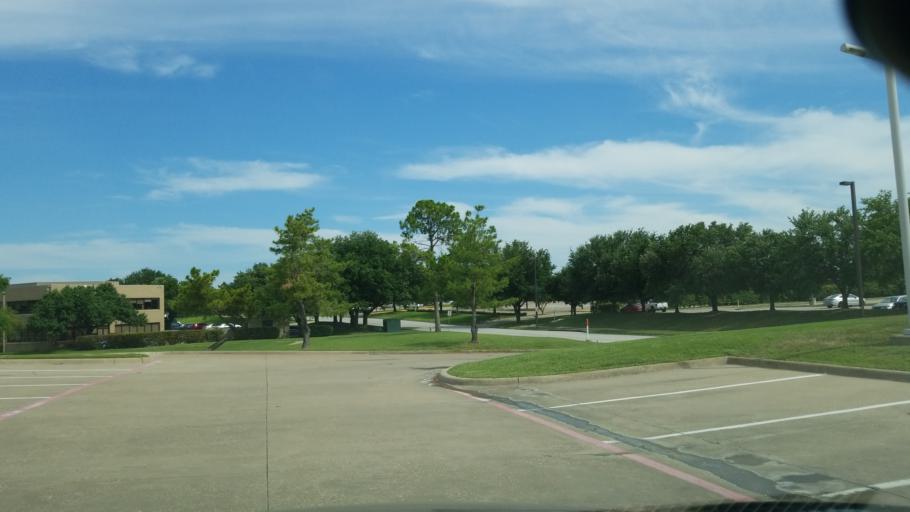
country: US
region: Texas
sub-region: Dallas County
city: Irving
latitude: 32.8829
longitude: -96.9778
